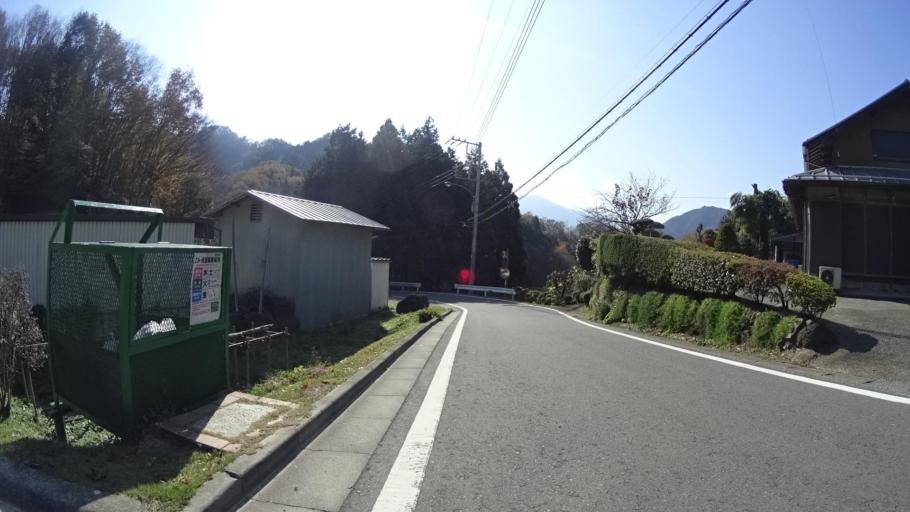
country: JP
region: Yamanashi
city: Uenohara
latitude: 35.5875
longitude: 139.1609
